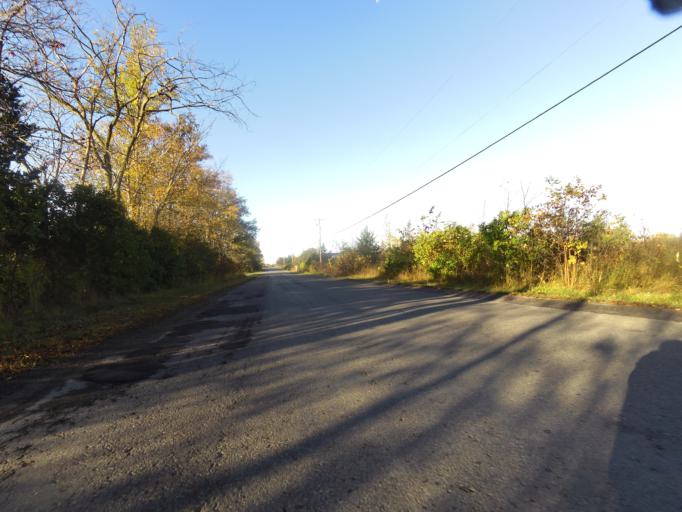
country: CA
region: Ontario
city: Belleville
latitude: 44.0360
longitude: -77.4603
